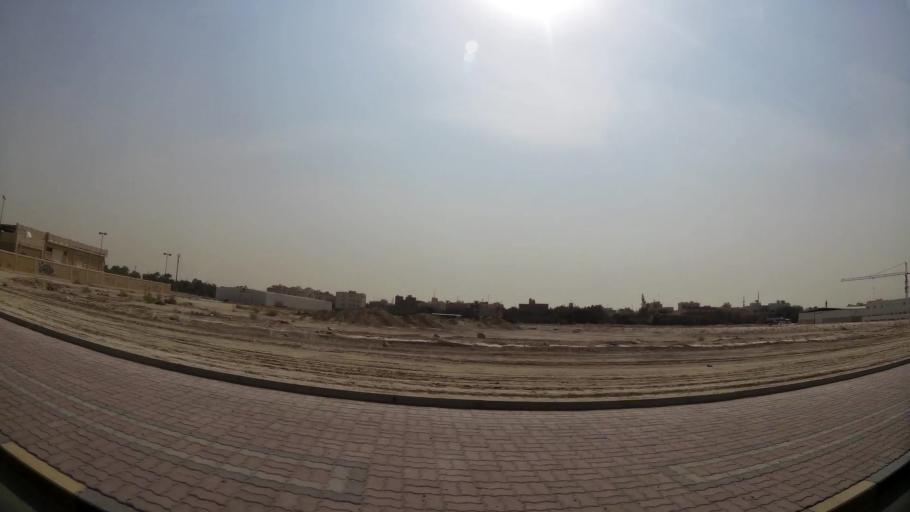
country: KW
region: Al Asimah
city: Ar Rabiyah
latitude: 29.3092
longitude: 47.8820
